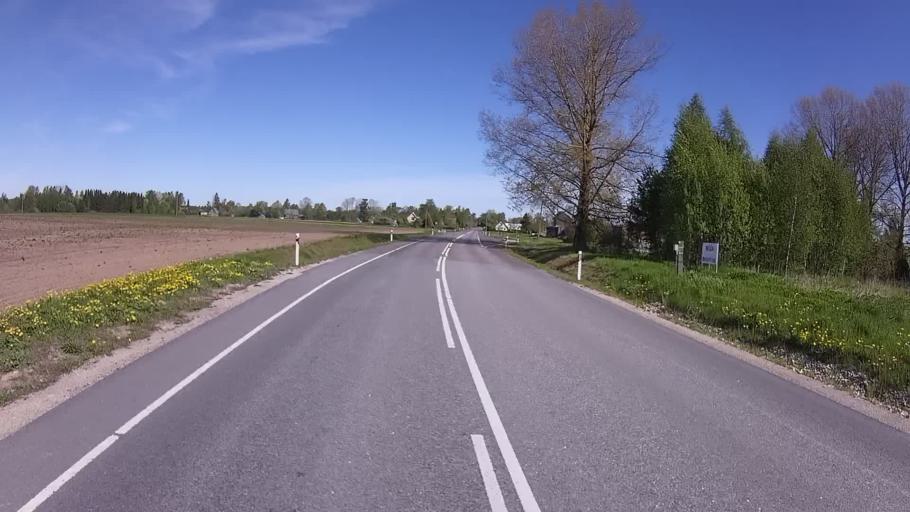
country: EE
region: Polvamaa
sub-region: Raepina vald
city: Rapina
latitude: 58.0697
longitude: 27.5438
